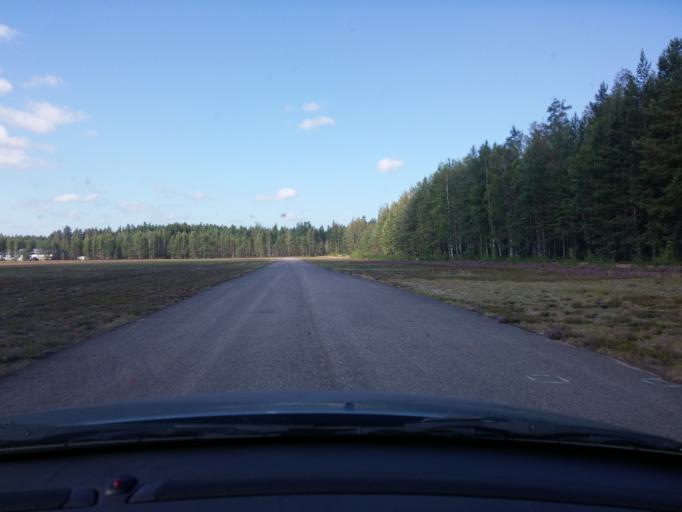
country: FI
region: Uusimaa
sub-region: Helsinki
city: Kaerkoelae
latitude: 60.7428
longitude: 24.0971
